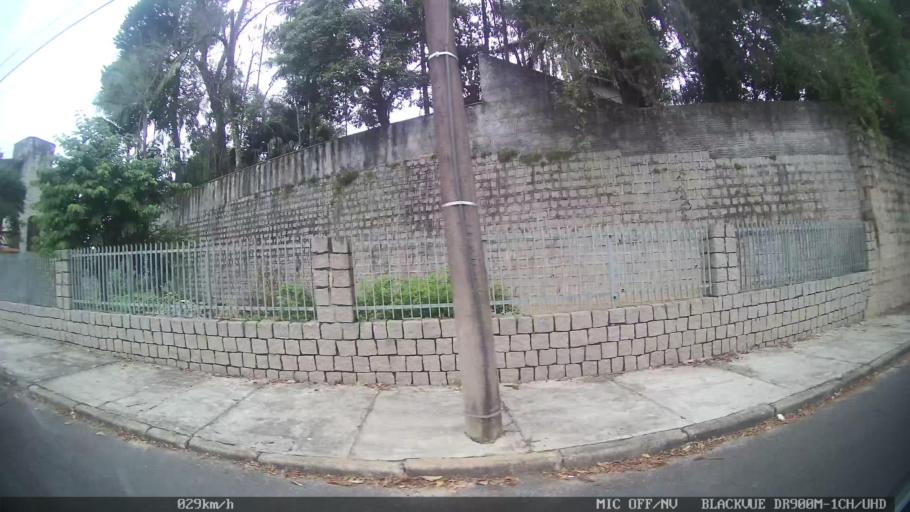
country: BR
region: Santa Catarina
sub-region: Joinville
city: Joinville
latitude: -26.2676
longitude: -48.8417
